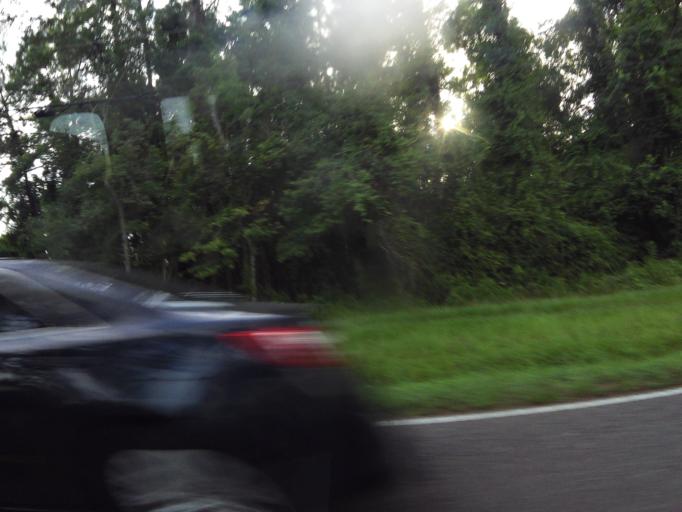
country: US
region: Florida
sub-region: Duval County
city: Jacksonville
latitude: 30.3830
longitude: -81.7731
